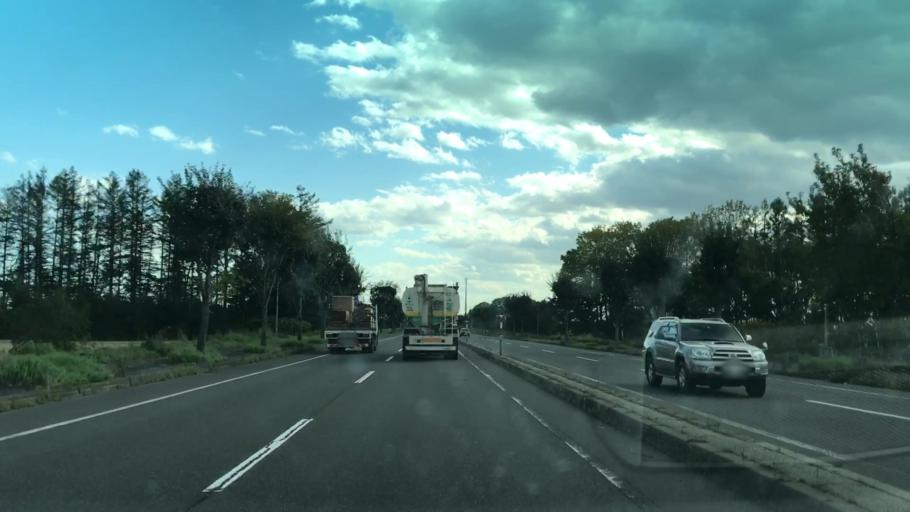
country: JP
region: Hokkaido
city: Otofuke
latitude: 43.0051
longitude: 143.1809
